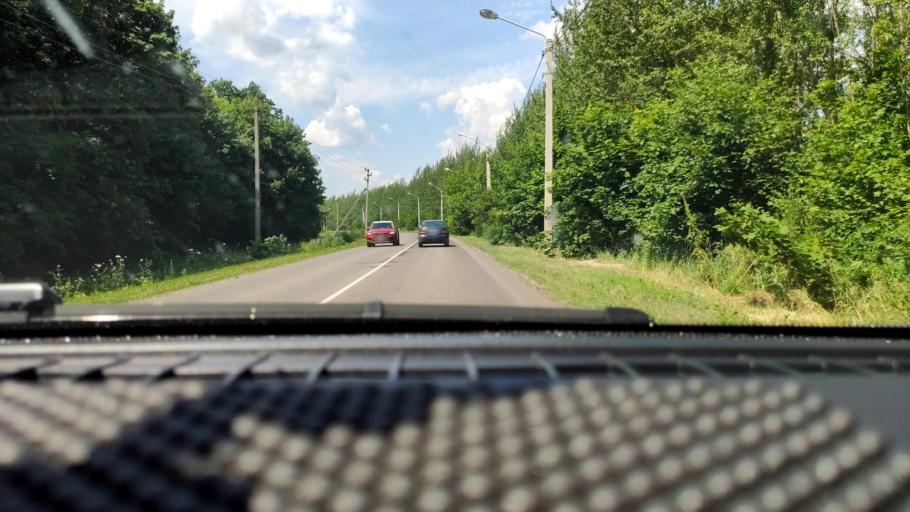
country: RU
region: Voronezj
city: Novaya Usman'
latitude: 51.6511
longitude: 39.4604
